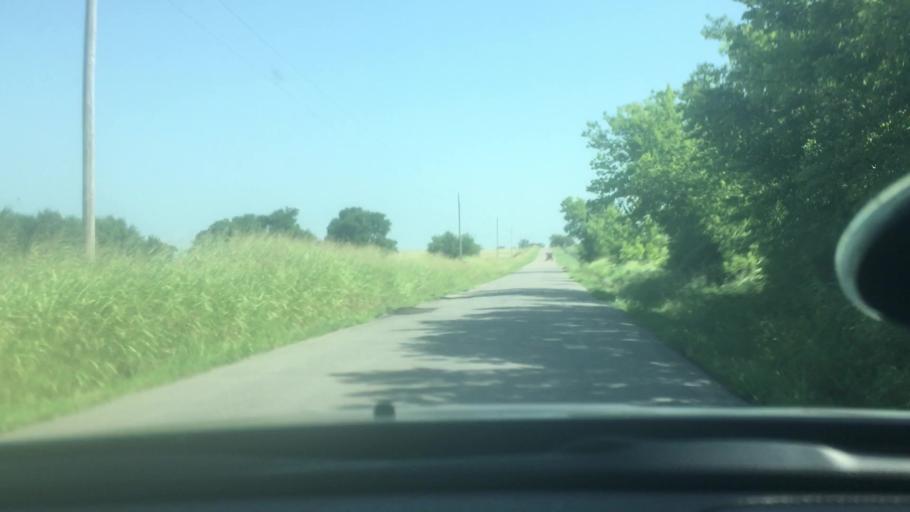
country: US
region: Oklahoma
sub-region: Bryan County
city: Calera
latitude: 33.9715
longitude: -96.4656
